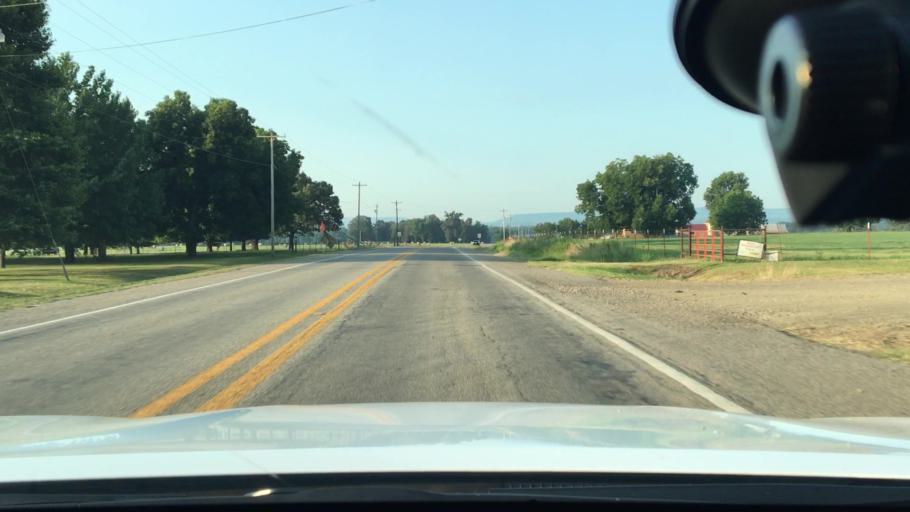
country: US
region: Arkansas
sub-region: Johnson County
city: Clarksville
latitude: 35.3844
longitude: -93.5296
